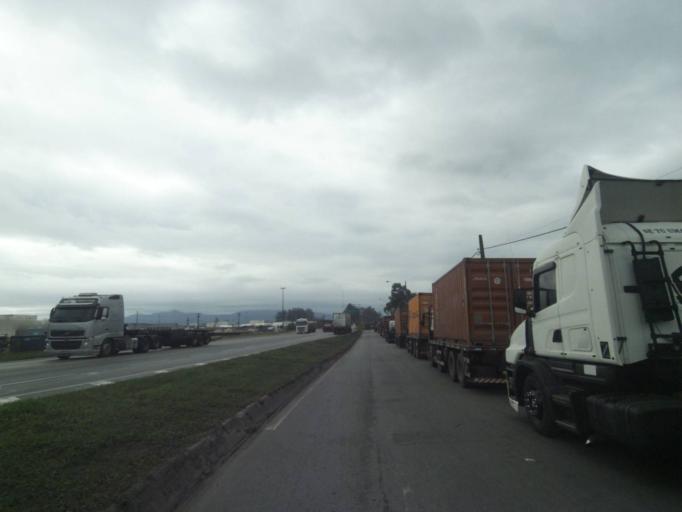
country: BR
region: Parana
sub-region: Paranagua
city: Paranagua
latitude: -25.5456
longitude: -48.5599
